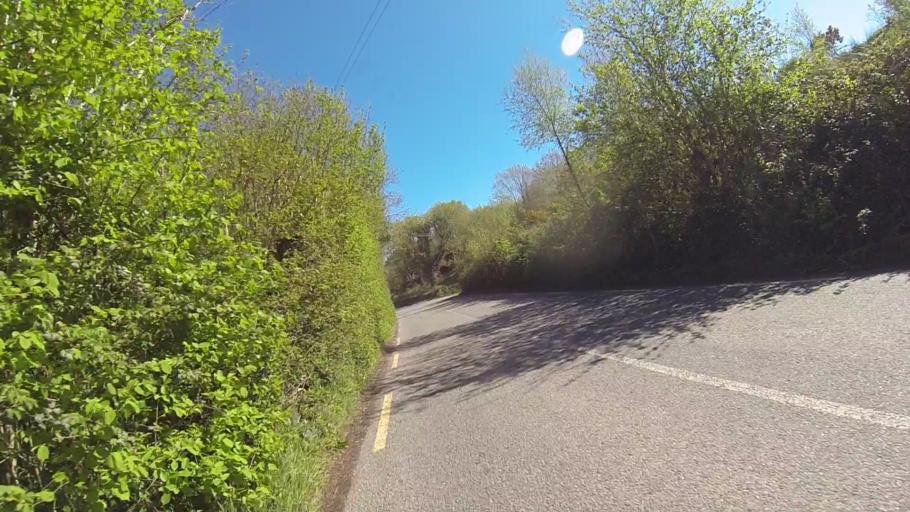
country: IE
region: Munster
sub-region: Ciarrai
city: Kenmare
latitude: 51.8565
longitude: -9.6226
